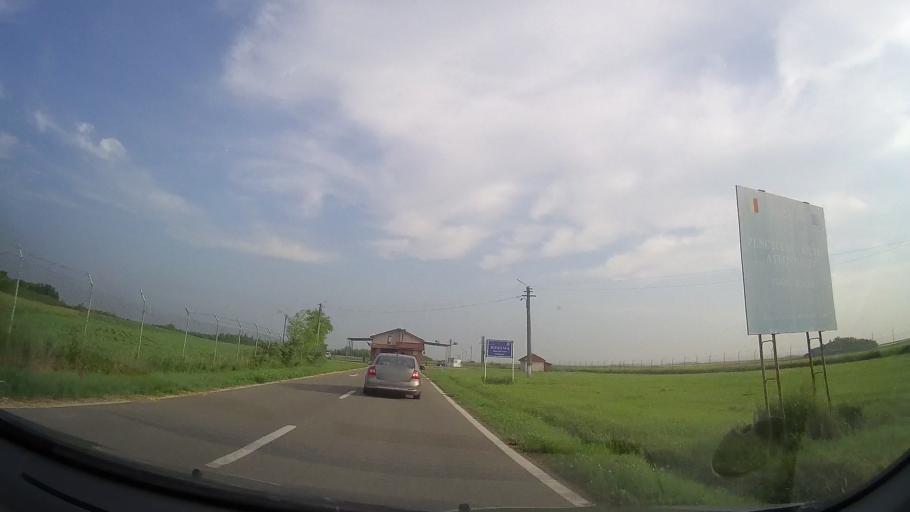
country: RS
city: Jasa Tomic
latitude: 45.4719
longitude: 20.8492
